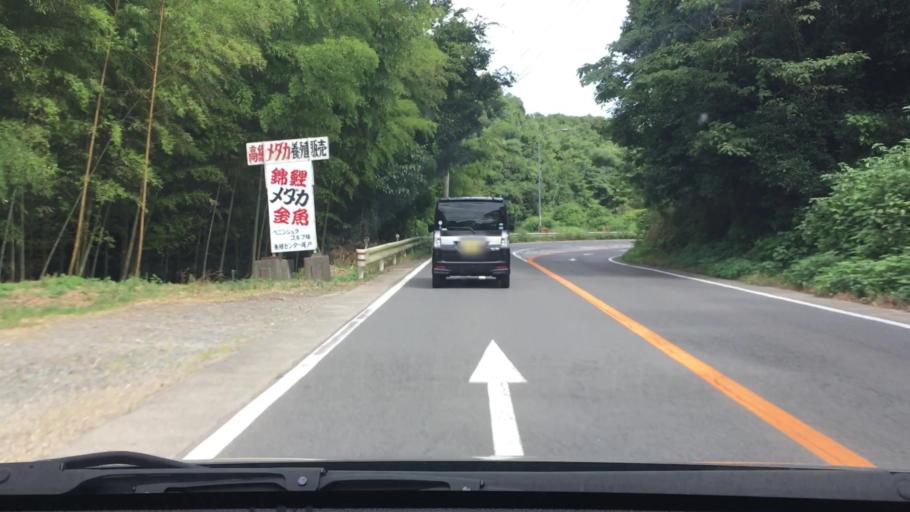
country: JP
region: Nagasaki
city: Togitsu
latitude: 32.9638
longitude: 129.7814
